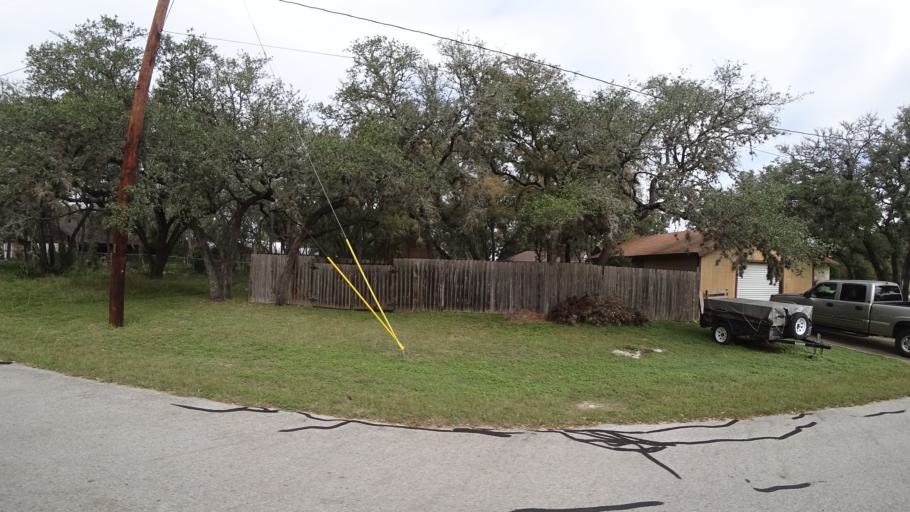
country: US
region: Texas
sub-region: Travis County
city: Shady Hollow
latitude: 30.1332
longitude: -97.8894
